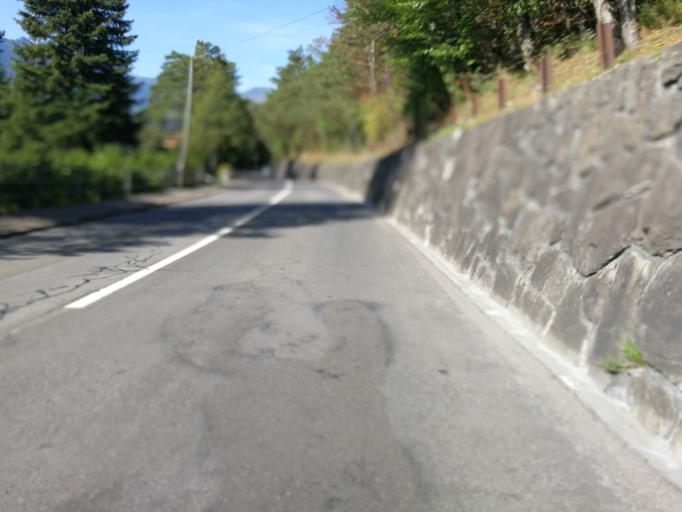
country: CH
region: Schwyz
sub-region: Bezirk Gersau
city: Gersau
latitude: 46.9906
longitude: 8.5528
